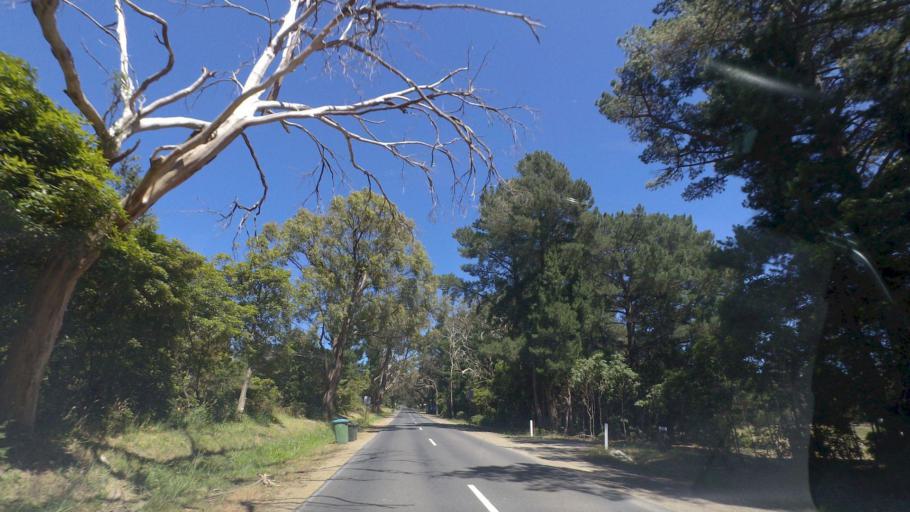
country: AU
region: Victoria
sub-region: Mornington Peninsula
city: Merricks
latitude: -38.3740
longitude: 145.0637
